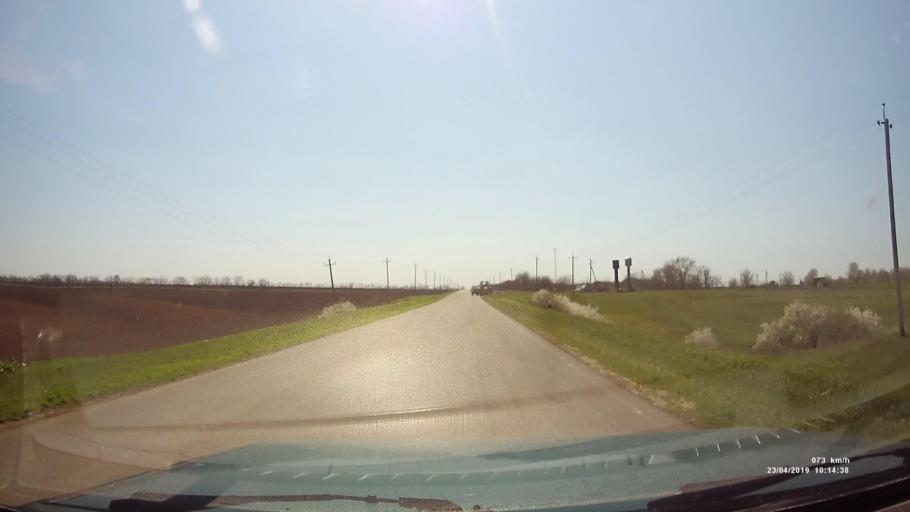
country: RU
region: Rostov
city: Sovetskoye
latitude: 46.6749
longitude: 42.3721
